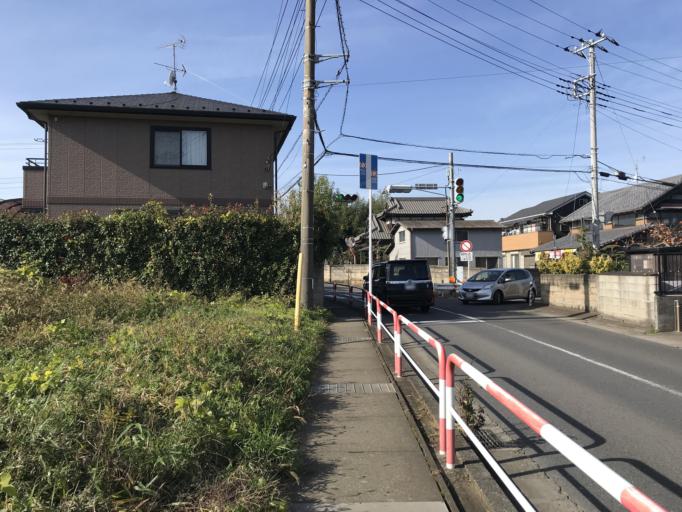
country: JP
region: Chiba
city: Shiroi
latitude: 35.7838
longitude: 139.9939
